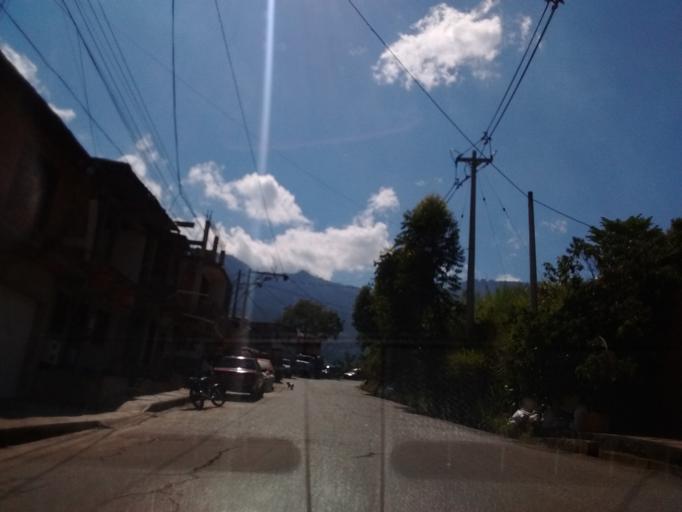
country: CO
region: Antioquia
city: Medellin
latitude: 6.2297
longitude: -75.5352
